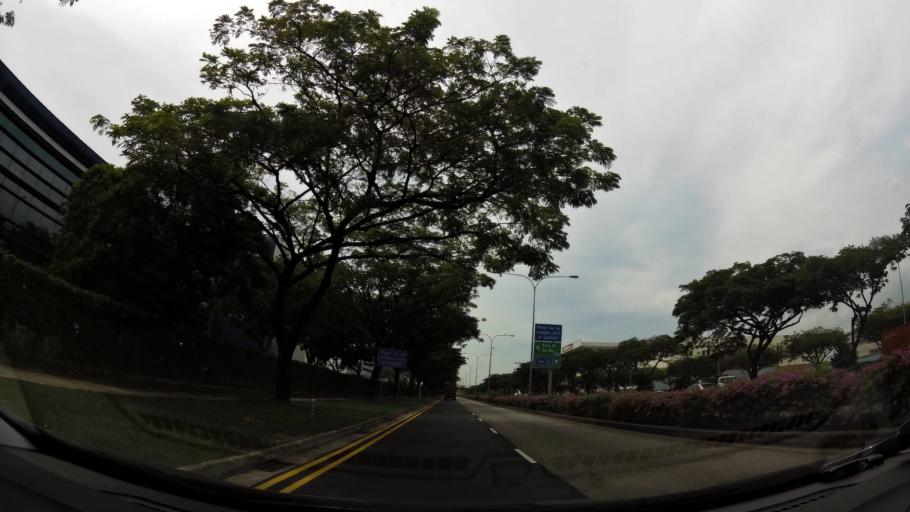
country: MY
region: Johor
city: Johor Bahru
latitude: 1.3225
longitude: 103.6894
